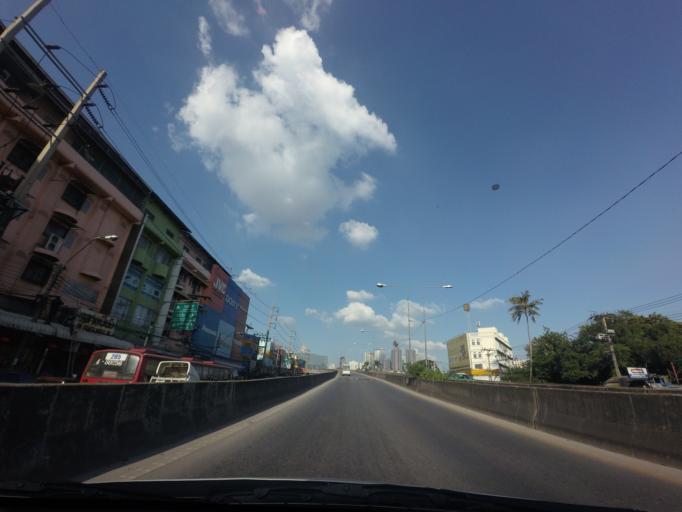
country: TH
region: Bangkok
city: Khlong Toei
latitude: 13.7165
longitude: 100.5571
